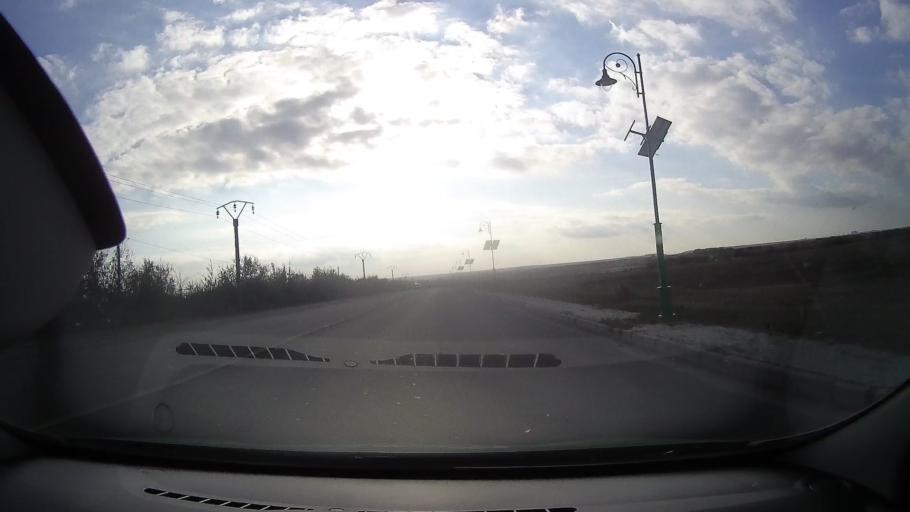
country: RO
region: Constanta
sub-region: Comuna Navodari
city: Navodari
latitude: 44.2898
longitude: 28.6086
